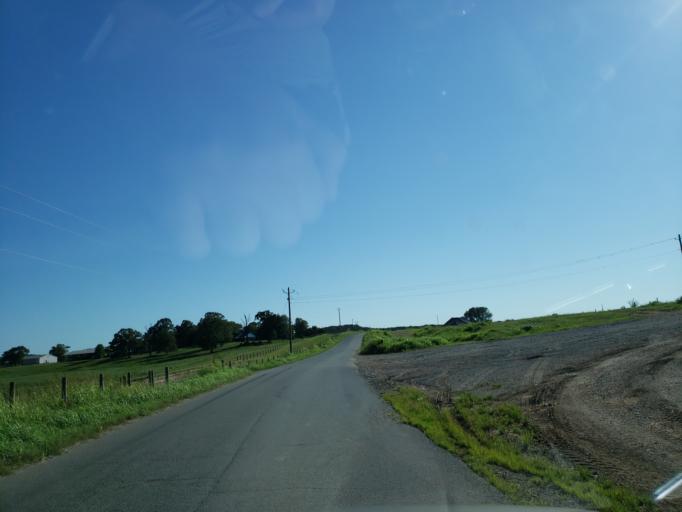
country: US
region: Georgia
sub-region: Bartow County
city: Euharlee
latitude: 34.0975
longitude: -84.9027
